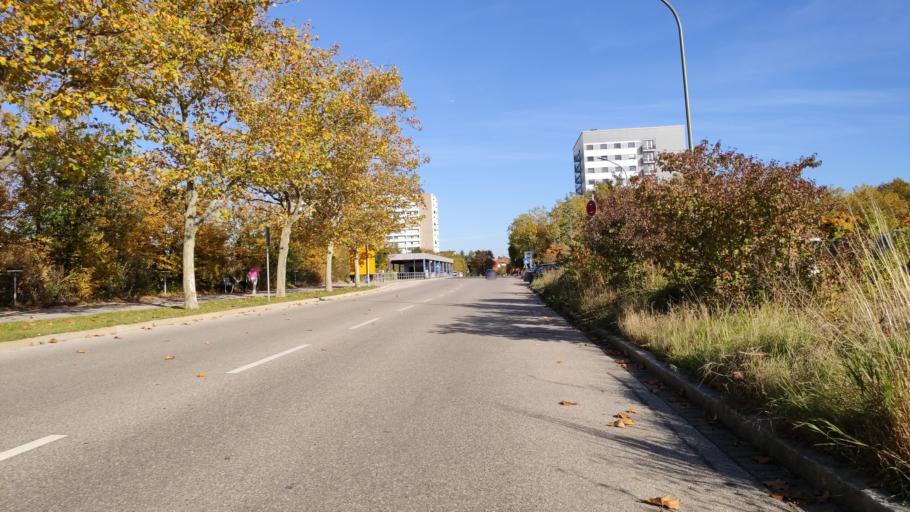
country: DE
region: Bavaria
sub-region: Upper Bavaria
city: Neuried
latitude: 48.1128
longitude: 11.4718
